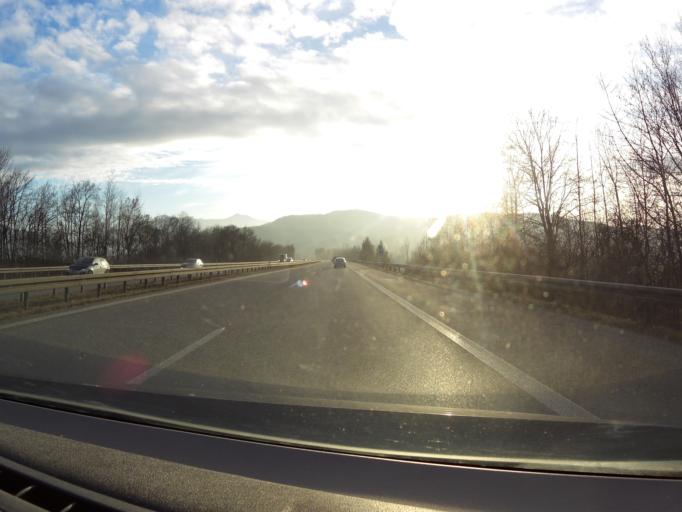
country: DE
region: Bavaria
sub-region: Upper Bavaria
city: Sindelsdorf
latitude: 47.7325
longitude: 11.3280
